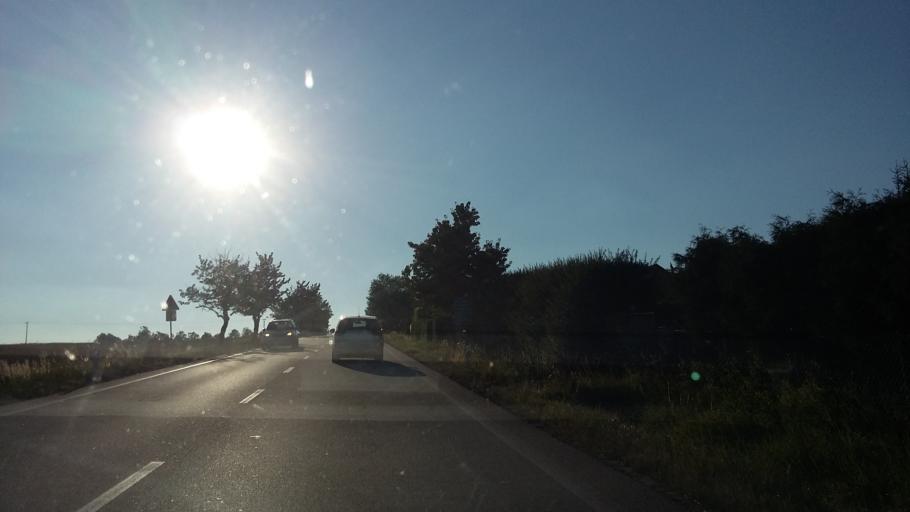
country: CZ
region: Vysocina
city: Velky Beranov
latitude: 49.4025
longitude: 15.6648
